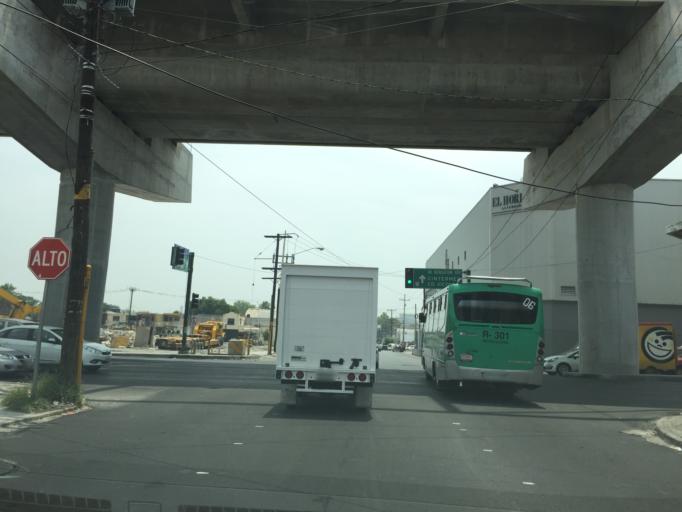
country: MX
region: Nuevo Leon
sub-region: Monterrey
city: Monterrey
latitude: 25.6779
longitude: -100.2980
